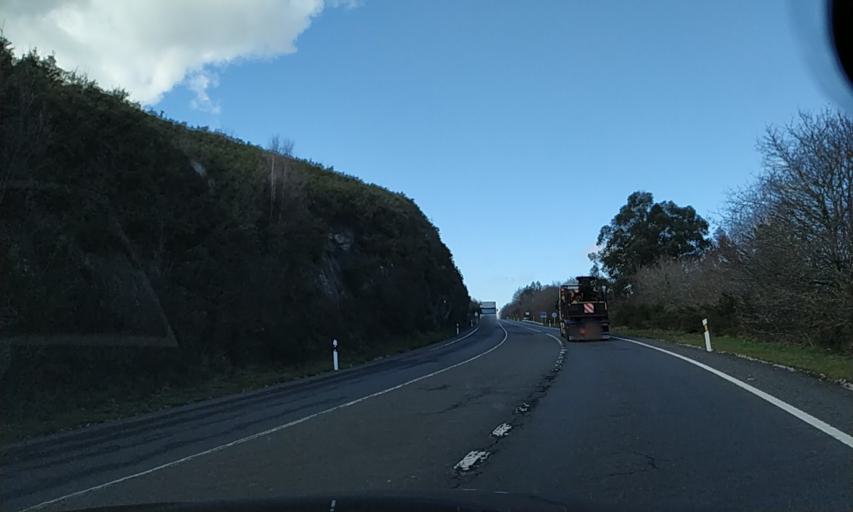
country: ES
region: Galicia
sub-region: Provincia de Pontevedra
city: Silleda
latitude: 42.7001
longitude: -8.3391
